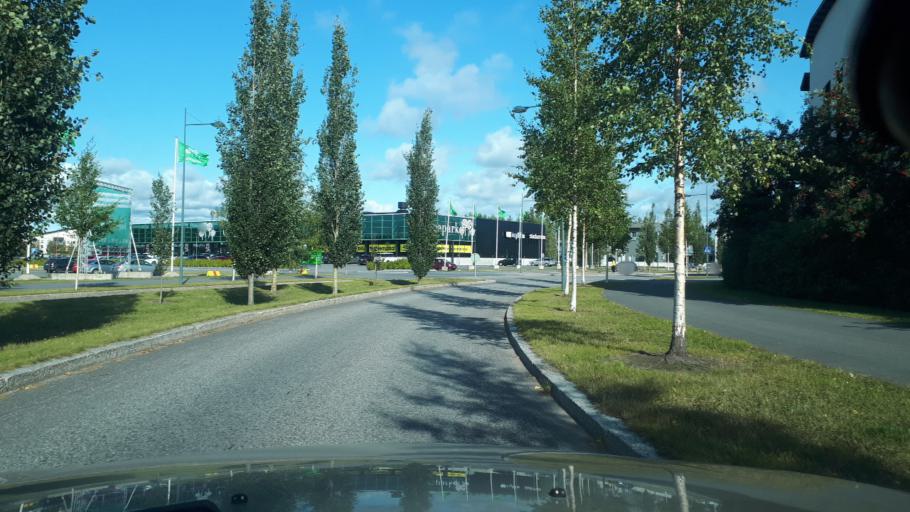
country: FI
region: Northern Ostrobothnia
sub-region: Oulu
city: Oulu
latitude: 65.0766
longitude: 25.4484
